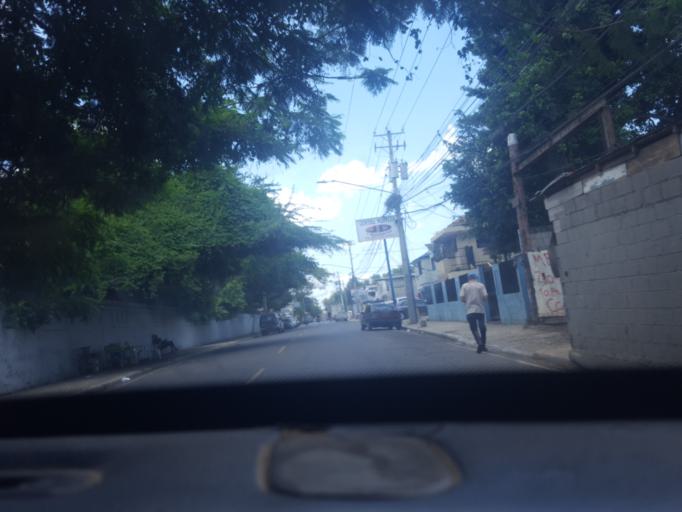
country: DO
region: Santiago
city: Santiago de los Caballeros
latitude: 19.4761
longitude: -70.7206
